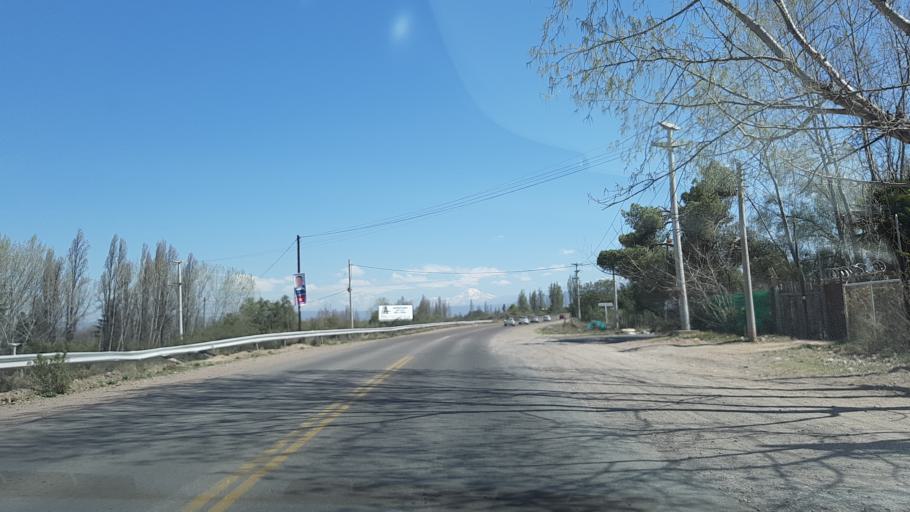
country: AR
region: Mendoza
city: Lujan de Cuyo
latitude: -33.0163
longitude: -68.9333
